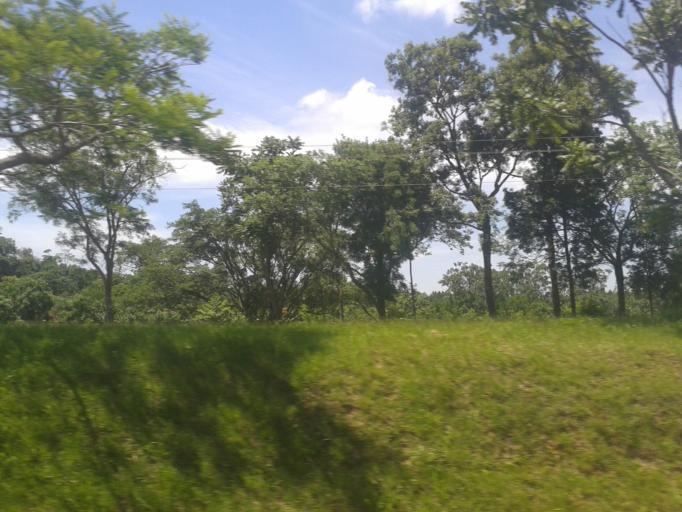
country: AR
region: Misiones
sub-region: Departamento de Leandro N. Alem
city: Leandro N. Alem
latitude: -27.6151
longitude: -55.2963
